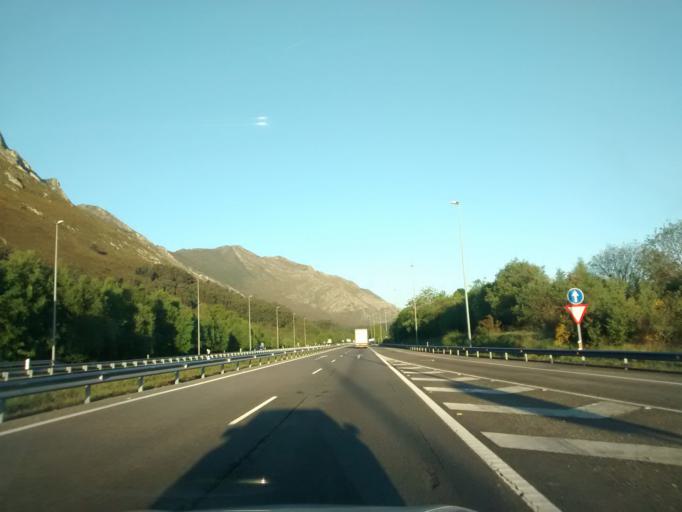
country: ES
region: Asturias
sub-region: Province of Asturias
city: Ribadesella
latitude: 43.4397
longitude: -4.9617
